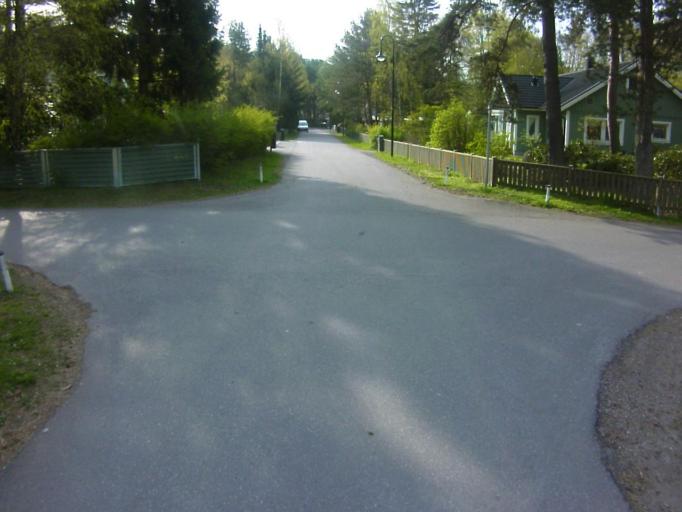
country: SE
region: Skane
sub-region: Kavlinge Kommun
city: Hofterup
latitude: 55.7600
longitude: 12.9777
